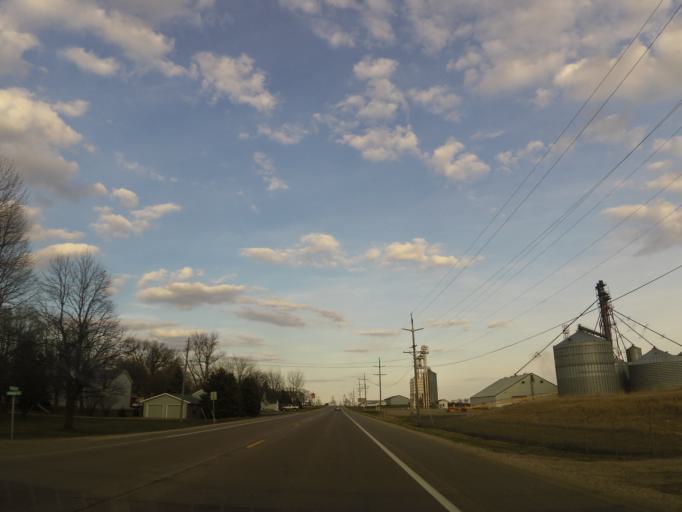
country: US
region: Minnesota
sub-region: McLeod County
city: Hutchinson
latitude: 44.7204
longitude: -94.4861
